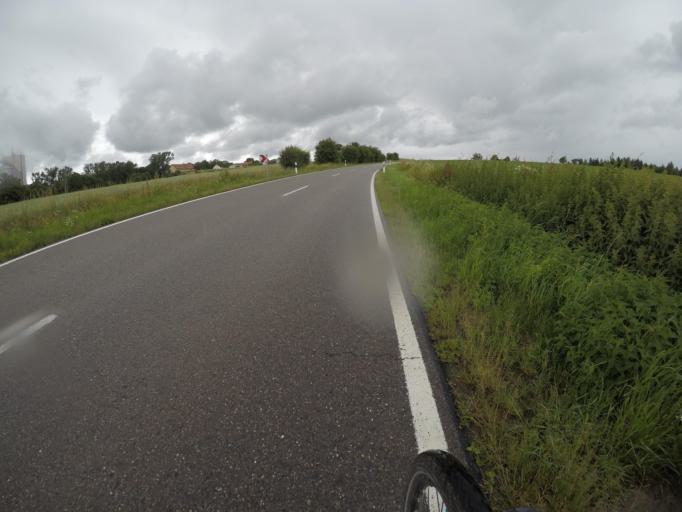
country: DE
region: Baden-Wuerttemberg
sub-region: Regierungsbezirk Stuttgart
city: Unterjettingen
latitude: 48.5687
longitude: 8.8161
